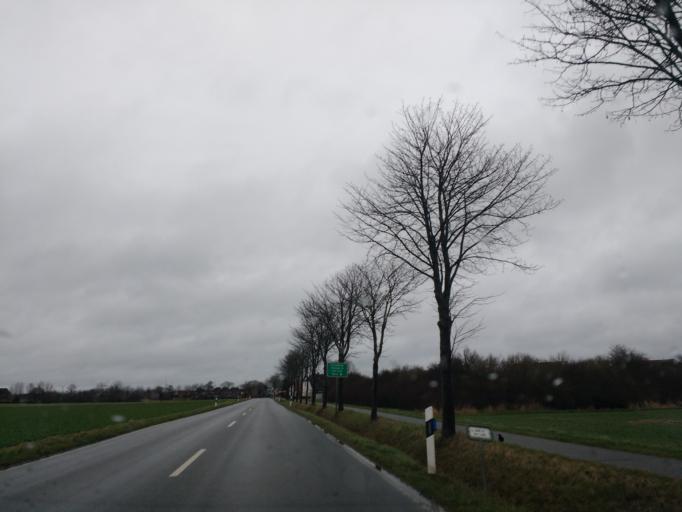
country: DE
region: Schleswig-Holstein
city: Fehmarn
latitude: 54.4538
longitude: 11.2076
